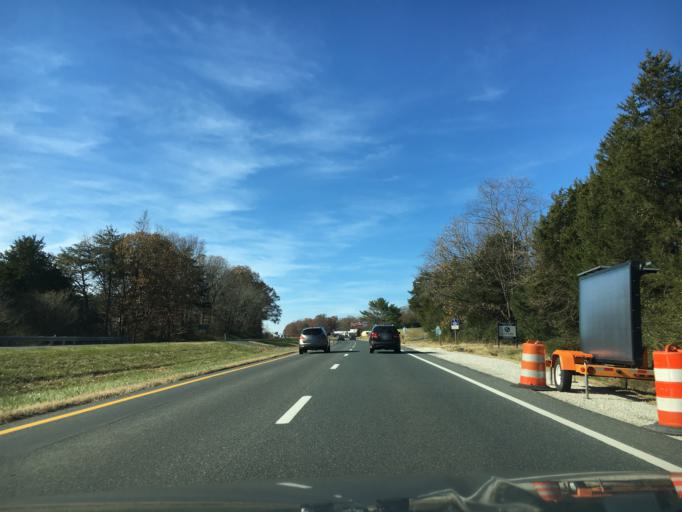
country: US
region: Virginia
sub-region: Campbell County
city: Concord
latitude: 37.3491
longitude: -78.9690
